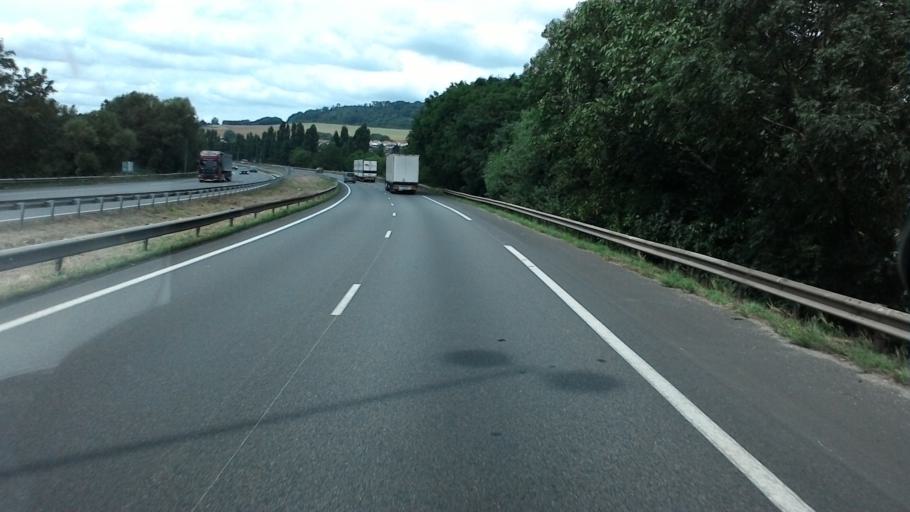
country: FR
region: Lorraine
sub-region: Departement de Meurthe-et-Moselle
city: Bouxieres-aux-Dames
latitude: 48.7514
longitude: 6.1571
